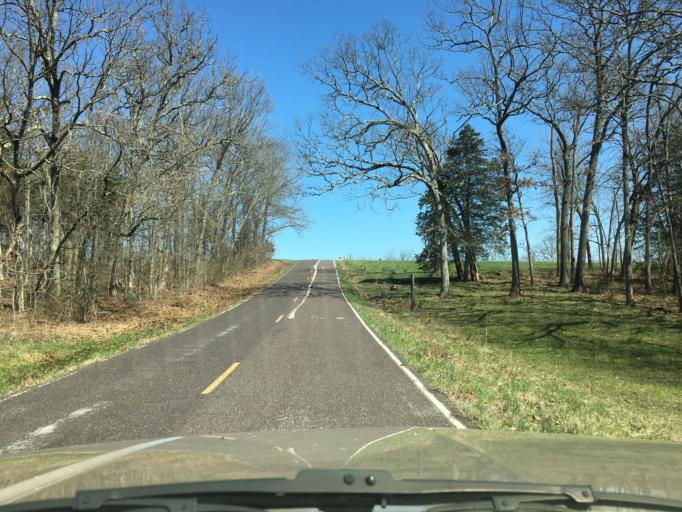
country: US
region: Missouri
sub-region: Franklin County
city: New Haven
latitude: 38.5509
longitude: -91.3303
